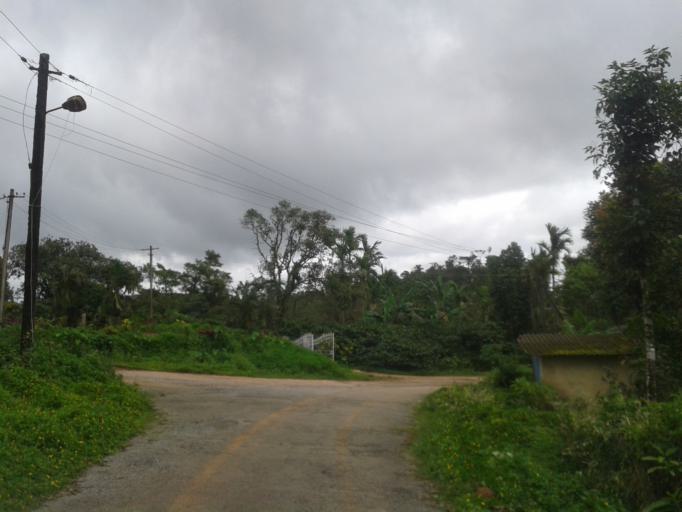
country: IN
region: Karnataka
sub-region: Chikmagalur
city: Mudigere
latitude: 12.9892
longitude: 75.6171
